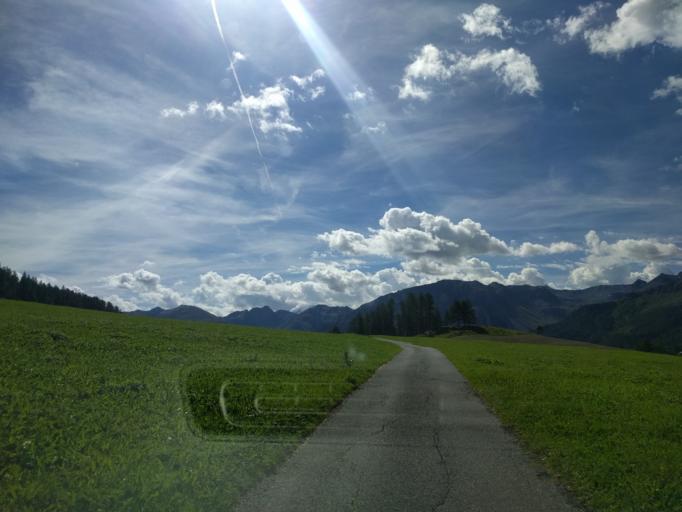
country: IT
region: Trentino-Alto Adige
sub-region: Bolzano
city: Tubre
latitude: 46.6244
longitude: 10.3629
